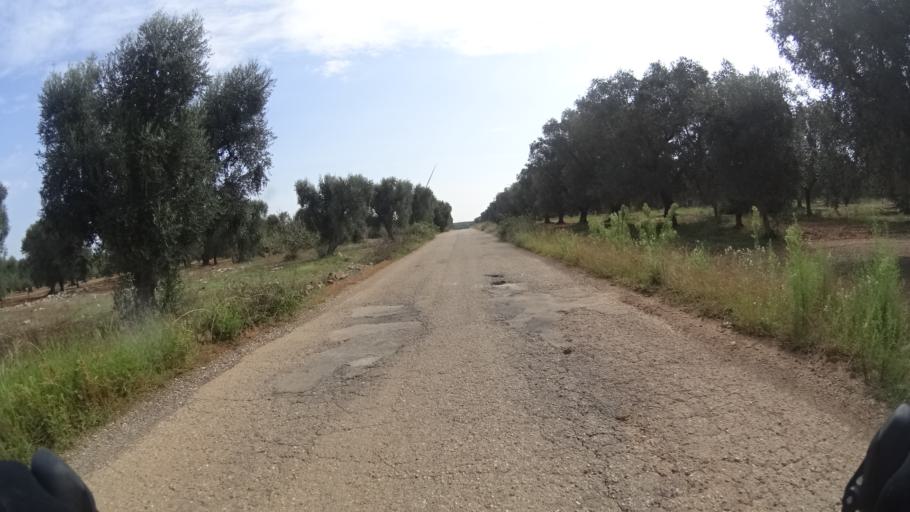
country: IT
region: Apulia
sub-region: Provincia di Taranto
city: San Marzano di San Giuseppe
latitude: 40.4382
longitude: 17.5349
